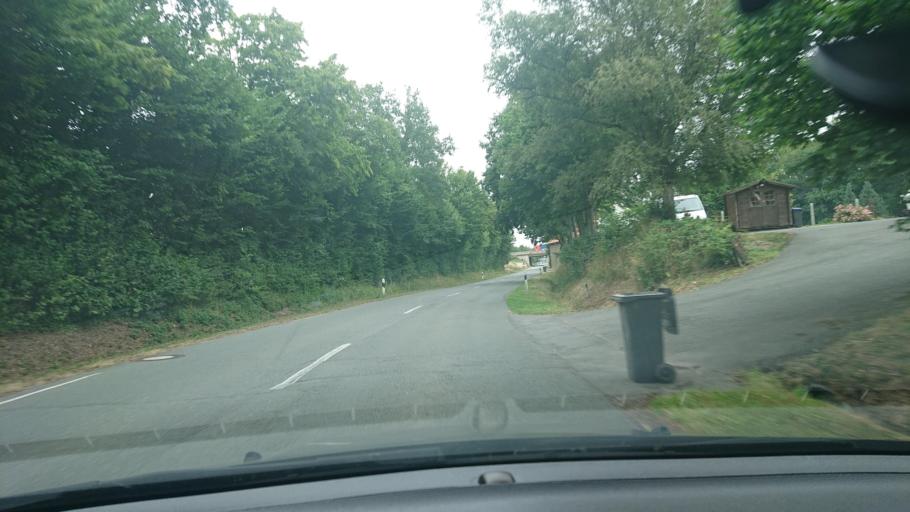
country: DE
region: North Rhine-Westphalia
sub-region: Regierungsbezirk Arnsberg
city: Bad Sassendorf
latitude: 51.5494
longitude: 8.1526
